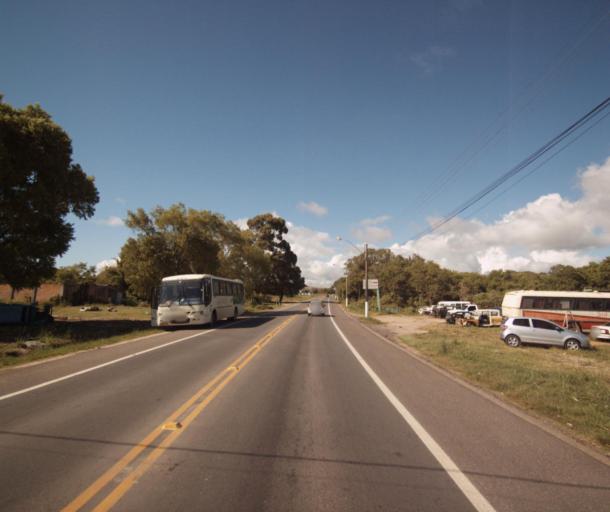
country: BR
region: Rio Grande do Sul
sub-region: Pelotas
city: Pelotas
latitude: -31.7598
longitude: -52.3562
